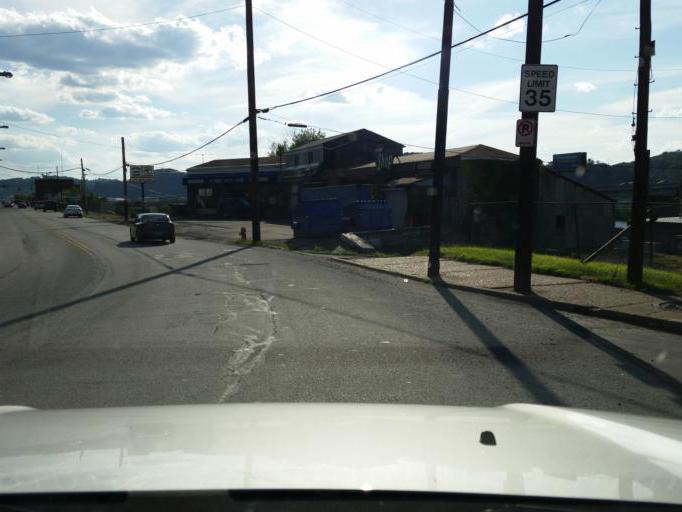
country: US
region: Pennsylvania
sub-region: Allegheny County
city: Sharpsburg
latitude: 40.4892
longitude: -79.9349
